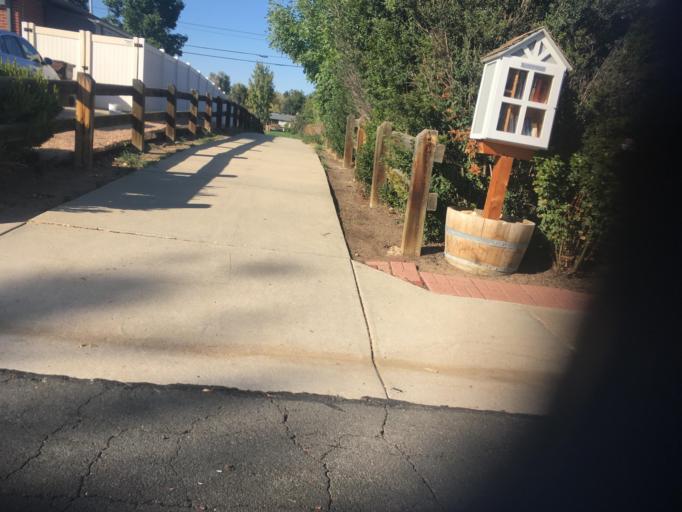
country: US
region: Colorado
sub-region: Broomfield County
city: Broomfield
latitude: 39.9215
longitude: -105.0823
